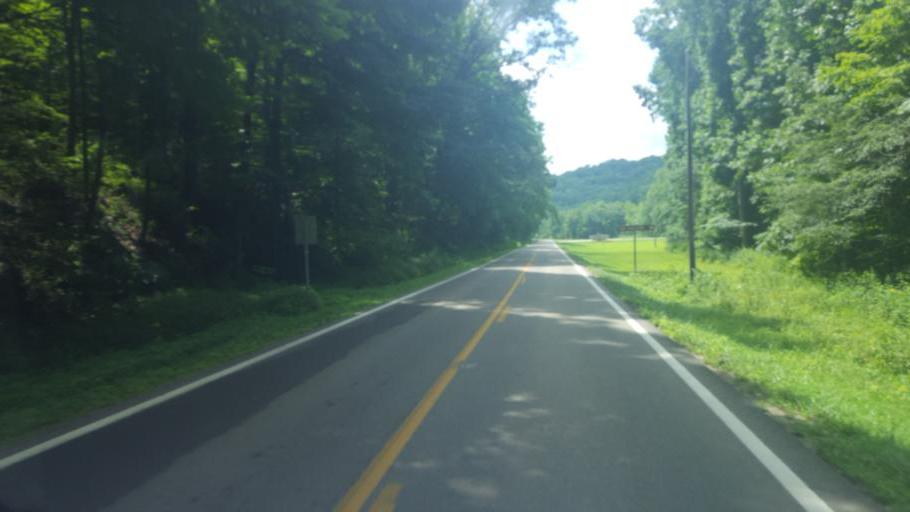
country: US
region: Ohio
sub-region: Ross County
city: Kingston
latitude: 39.3766
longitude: -82.7290
